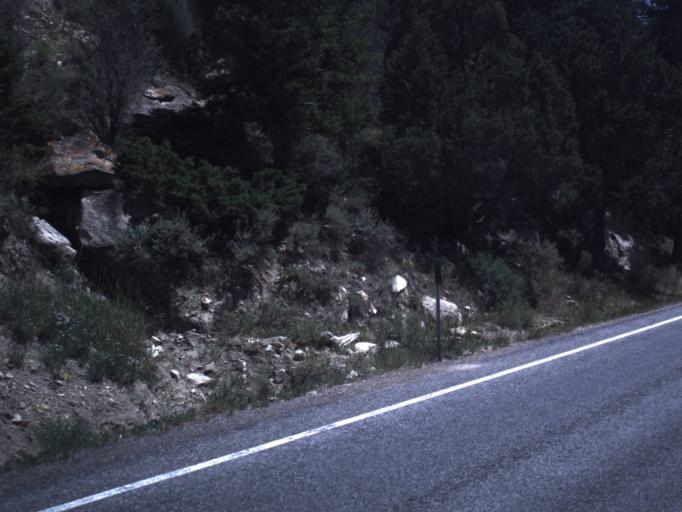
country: US
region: Utah
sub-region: Emery County
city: Huntington
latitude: 39.4493
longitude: -111.1394
